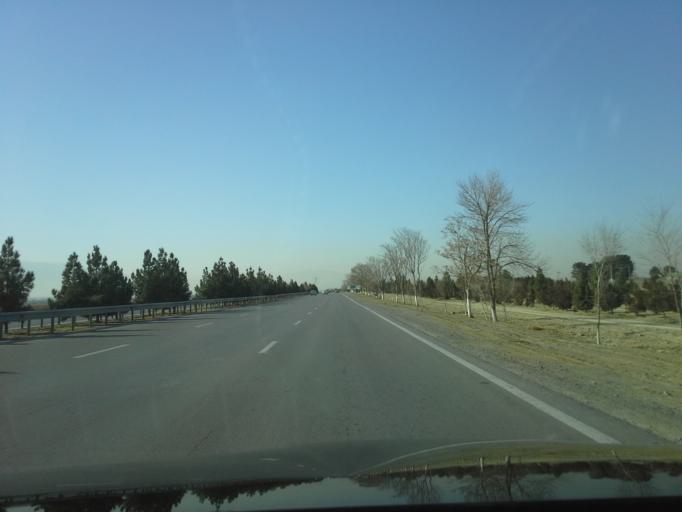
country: TM
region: Ahal
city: Annau
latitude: 37.9055
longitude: 58.5353
